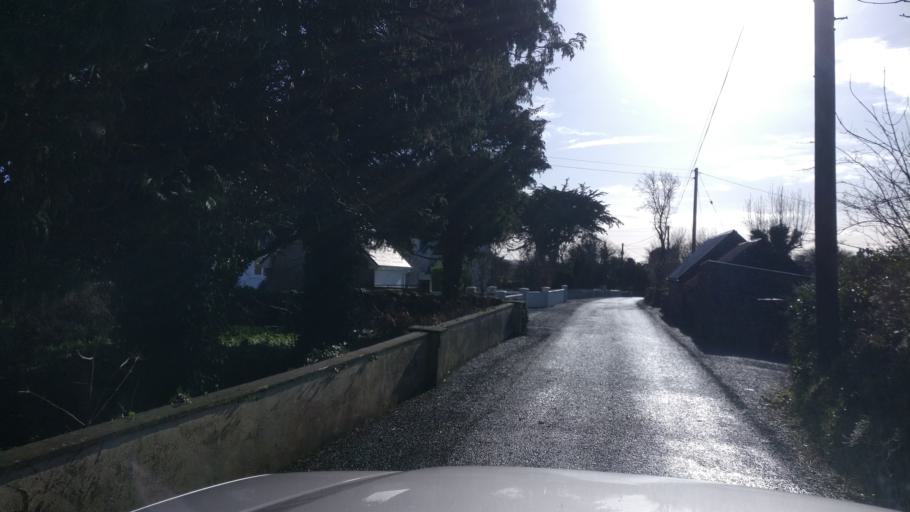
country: IE
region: Connaught
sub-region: County Galway
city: Athenry
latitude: 53.2337
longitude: -8.7795
